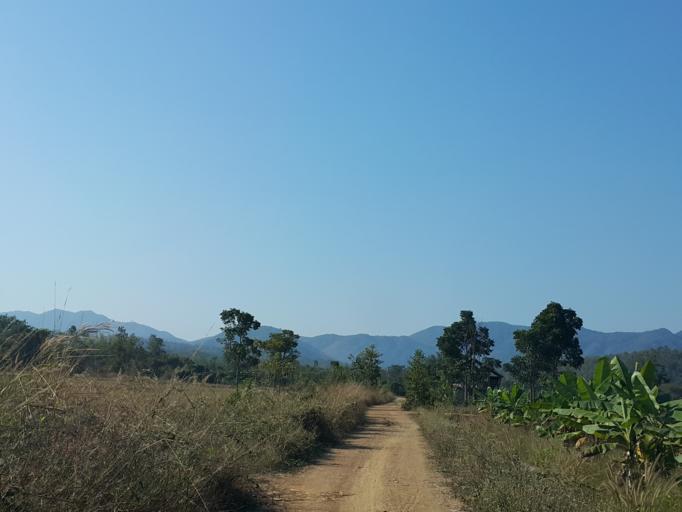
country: TH
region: Sukhothai
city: Thung Saliam
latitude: 17.3141
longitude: 99.4354
